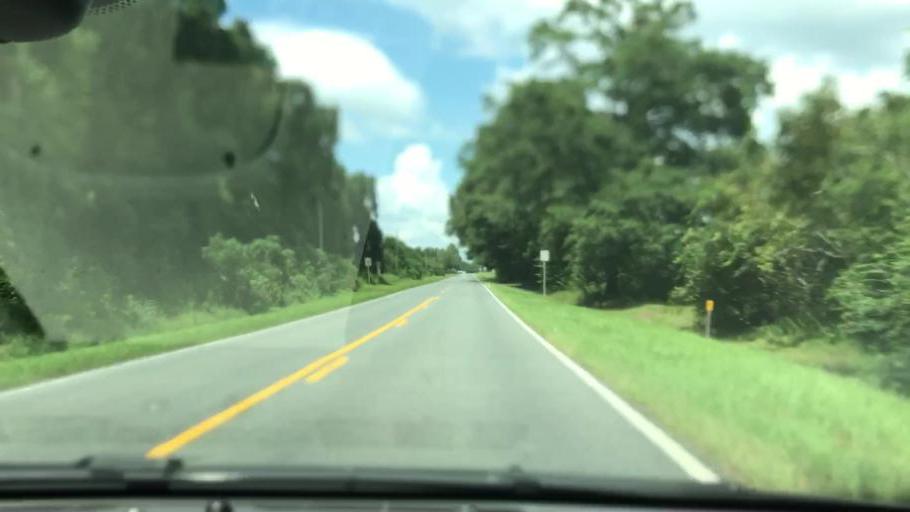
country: US
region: Florida
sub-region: Jackson County
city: Malone
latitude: 30.9193
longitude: -85.1187
